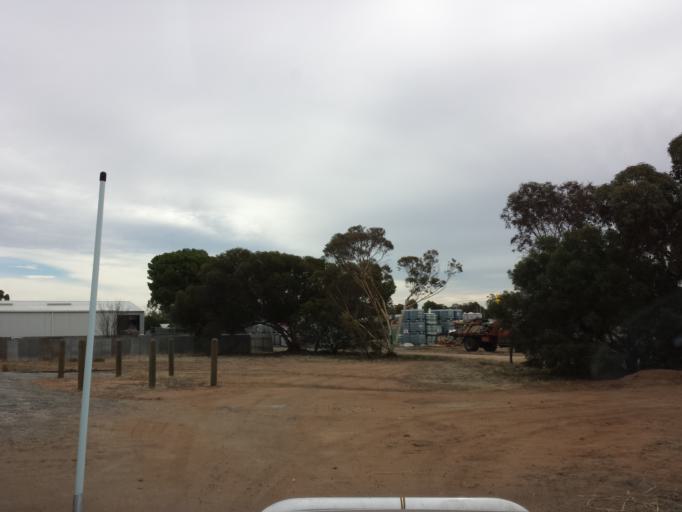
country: AU
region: Victoria
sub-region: Horsham
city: Horsham
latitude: -36.0758
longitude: 142.4166
